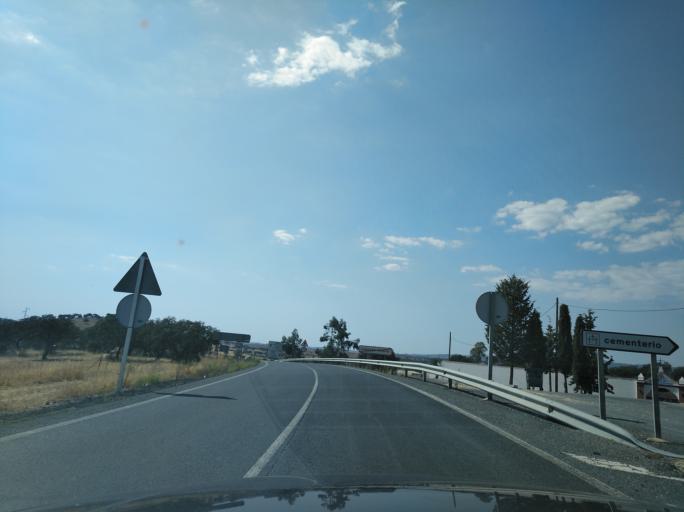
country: ES
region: Andalusia
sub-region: Provincia de Huelva
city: Cabezas Rubias
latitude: 37.7286
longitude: -7.0902
